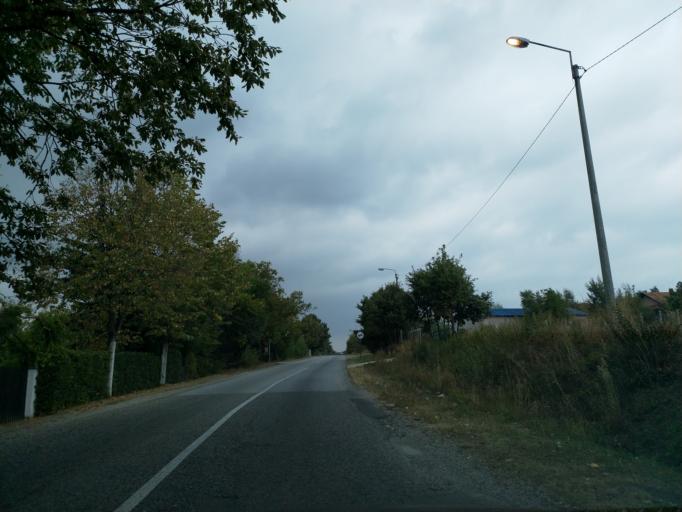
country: RS
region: Central Serbia
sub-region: Pomoravski Okrug
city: Jagodina
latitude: 44.0082
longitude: 21.2030
